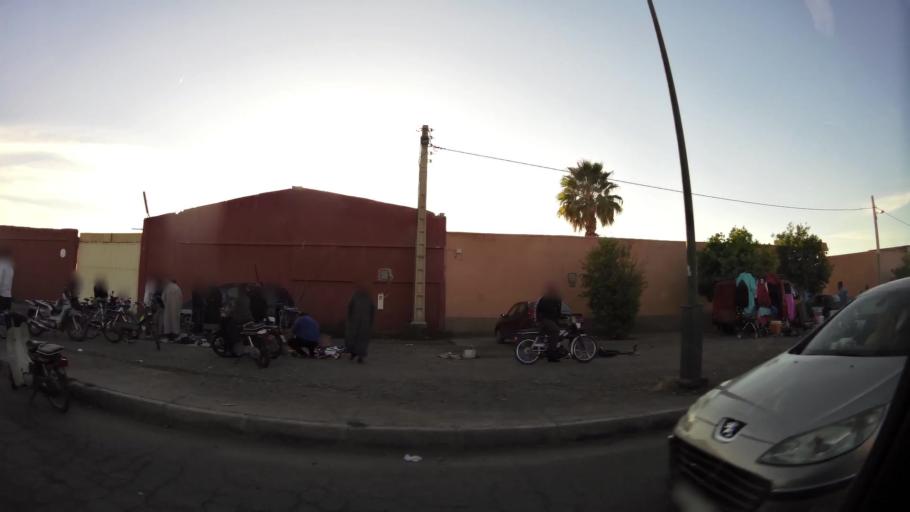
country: MA
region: Marrakech-Tensift-Al Haouz
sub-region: Marrakech
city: Marrakesh
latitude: 31.6233
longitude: -8.0436
